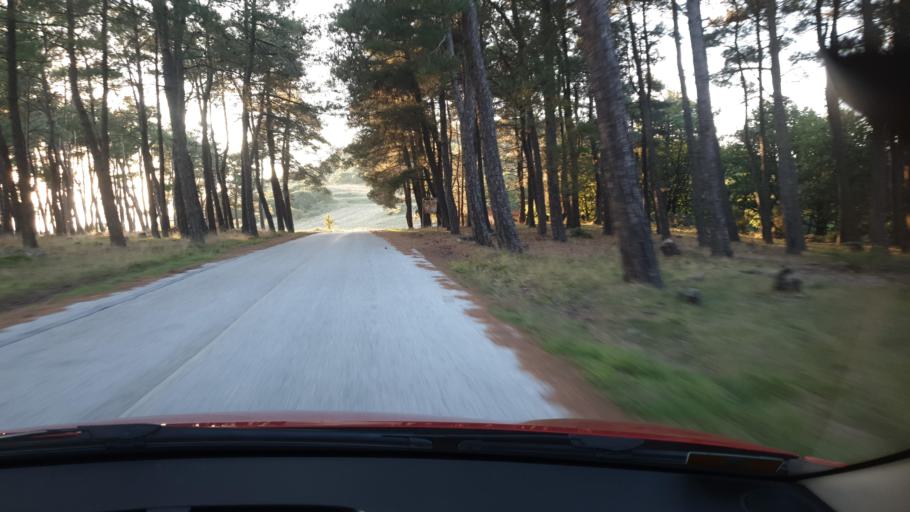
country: GR
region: Central Macedonia
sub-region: Nomos Thessalonikis
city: Peristera
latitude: 40.5128
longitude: 23.2160
